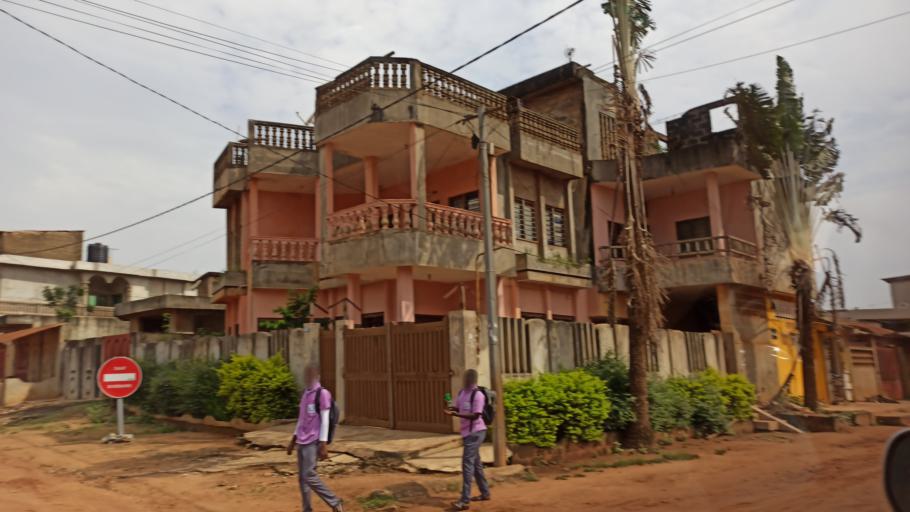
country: BJ
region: Queme
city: Porto-Novo
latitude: 6.5142
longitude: 2.6066
